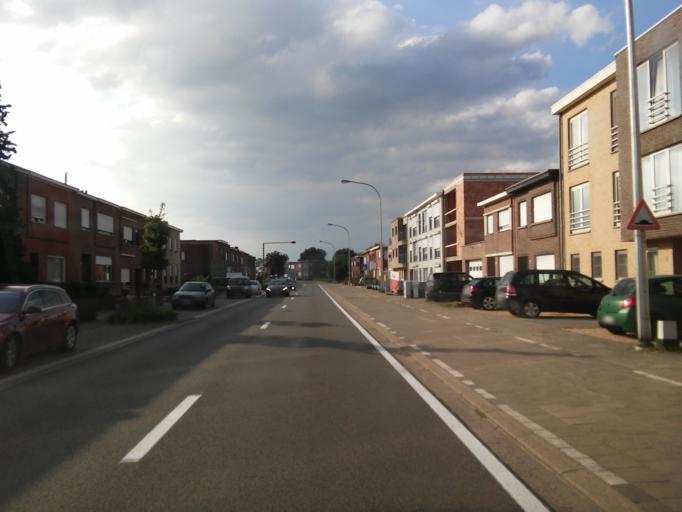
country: BE
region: Flanders
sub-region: Provincie Antwerpen
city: Duffel
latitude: 51.1011
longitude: 4.5046
